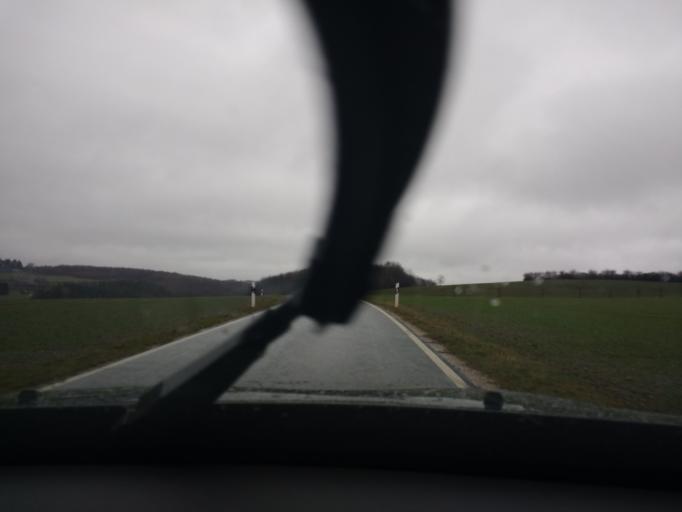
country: DE
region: Rheinland-Pfalz
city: Paschel
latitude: 49.6302
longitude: 6.6894
